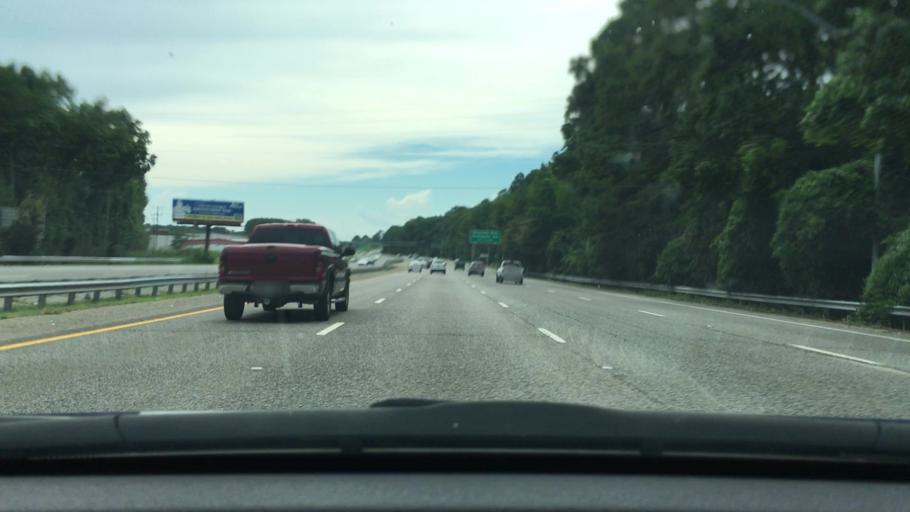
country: US
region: South Carolina
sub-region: Lexington County
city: West Columbia
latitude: 34.0108
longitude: -81.0652
